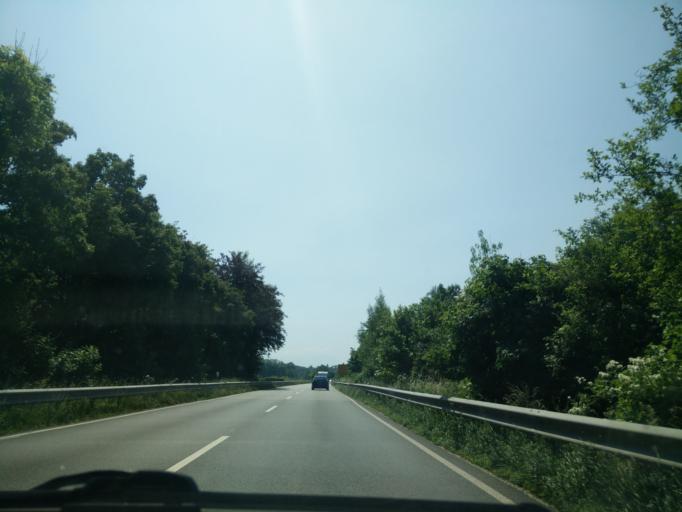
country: DE
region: Bavaria
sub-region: Upper Bavaria
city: Freilassing
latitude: 47.8850
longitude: 12.9669
